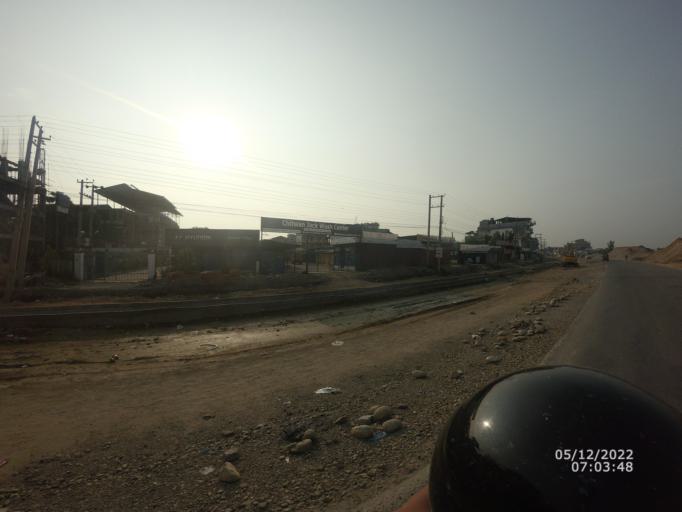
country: NP
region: Central Region
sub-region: Narayani Zone
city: Bharatpur
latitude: 27.6748
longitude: 84.4314
